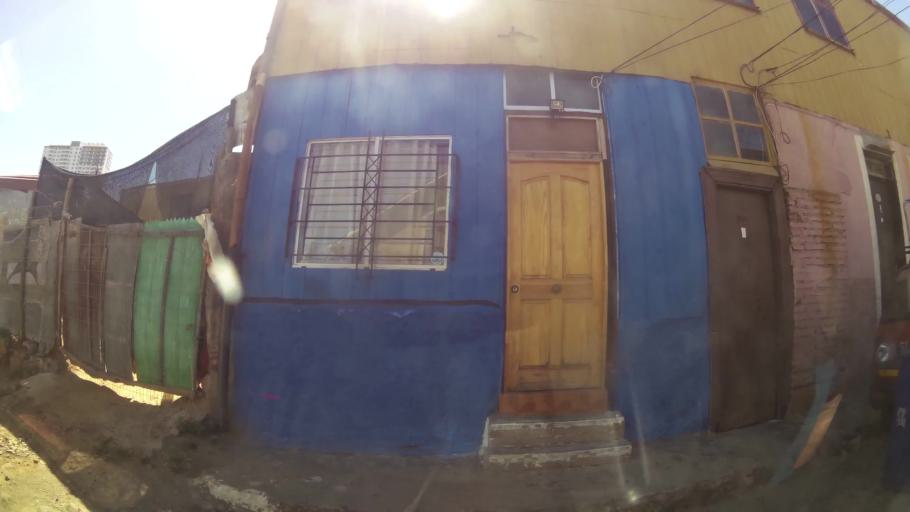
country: CL
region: Valparaiso
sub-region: Provincia de Valparaiso
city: Valparaiso
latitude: -33.0516
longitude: -71.5986
